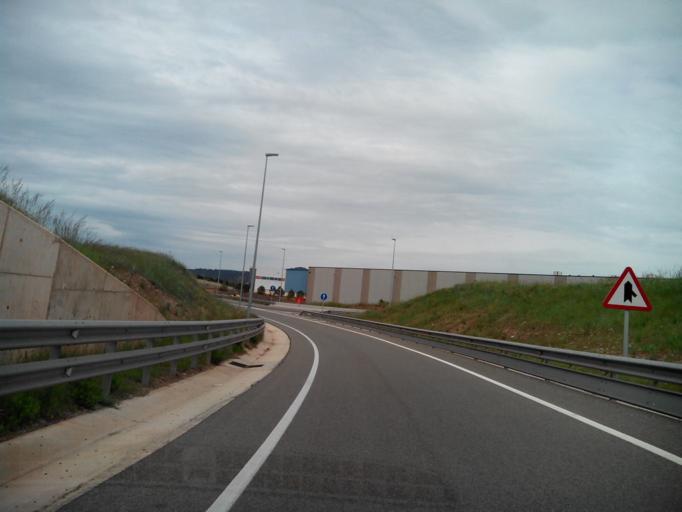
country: ES
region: Catalonia
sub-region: Provincia de Barcelona
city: Navarcles
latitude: 41.7801
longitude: 1.8889
